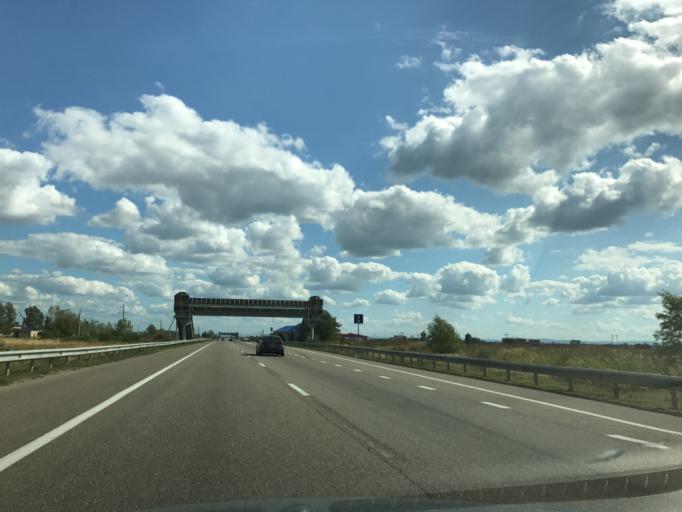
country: RU
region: Adygeya
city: Adygeysk
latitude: 44.8830
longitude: 39.1756
